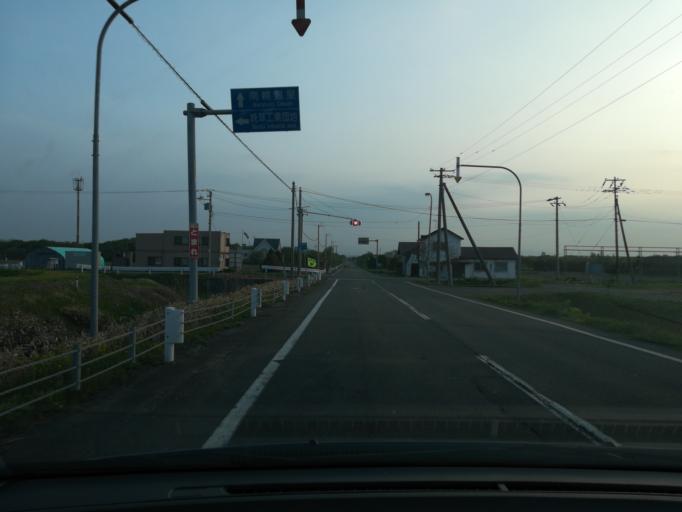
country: JP
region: Hokkaido
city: Ebetsu
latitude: 43.0750
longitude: 141.6030
